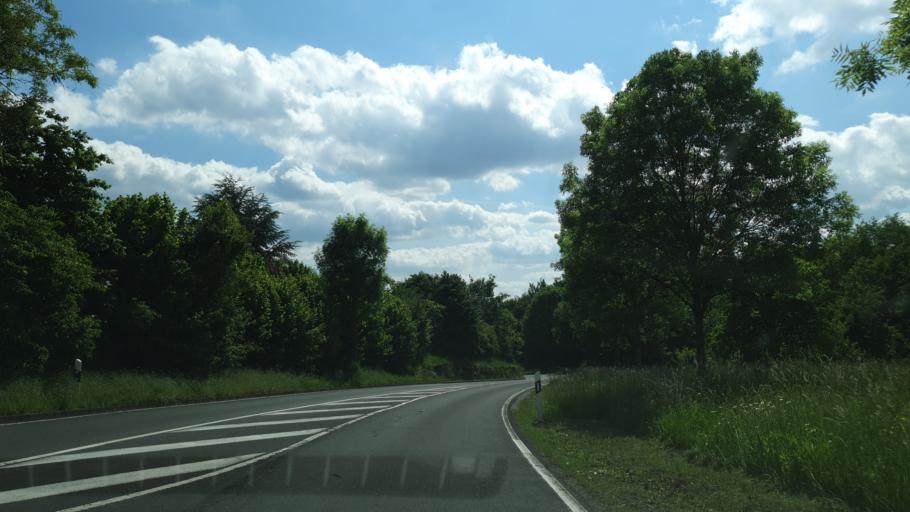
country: DE
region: Rheinland-Pfalz
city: Mogendorf
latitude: 50.4885
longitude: 7.7806
